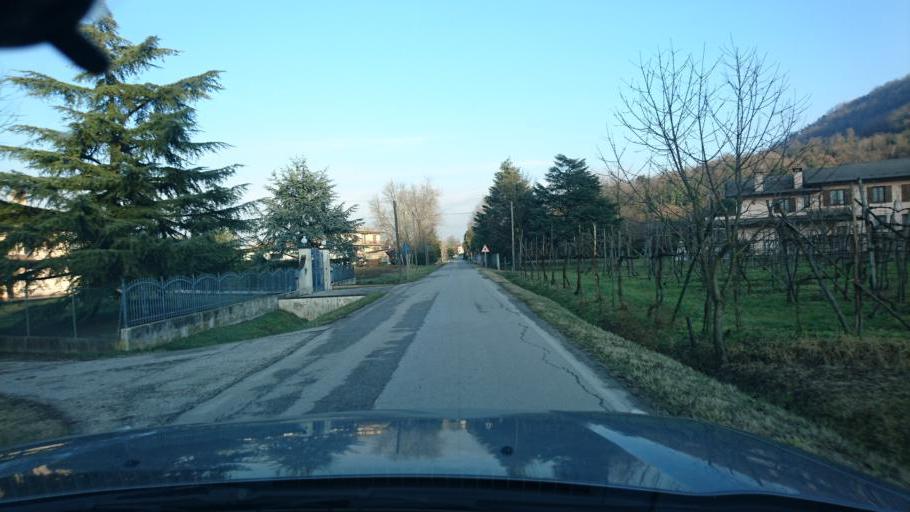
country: IT
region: Veneto
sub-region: Provincia di Padova
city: Torreglia
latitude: 45.3257
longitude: 11.7542
